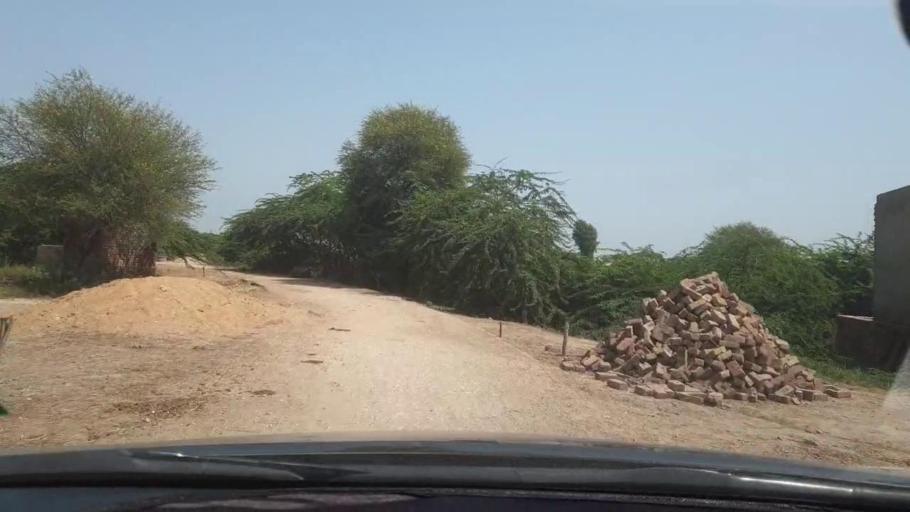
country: PK
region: Sindh
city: Naukot
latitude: 24.7802
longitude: 69.1917
